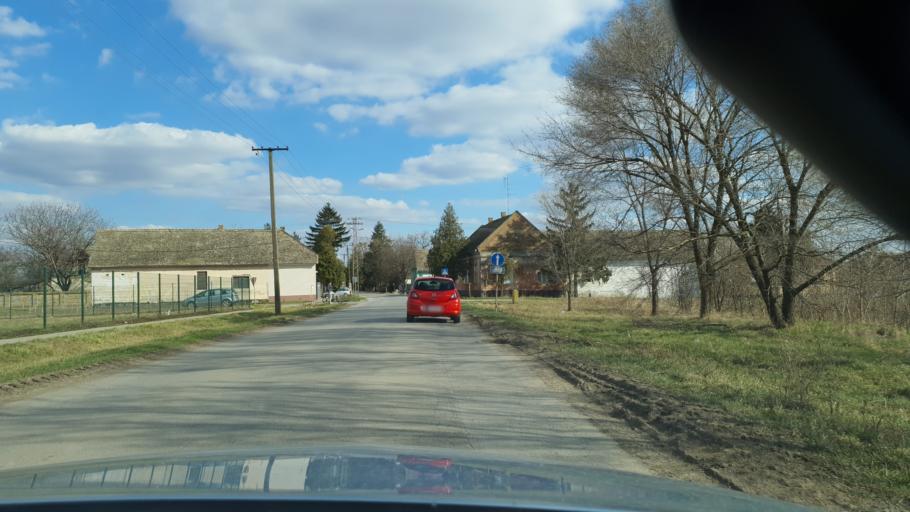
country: RS
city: Zmajevo
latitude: 45.4570
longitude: 19.6792
